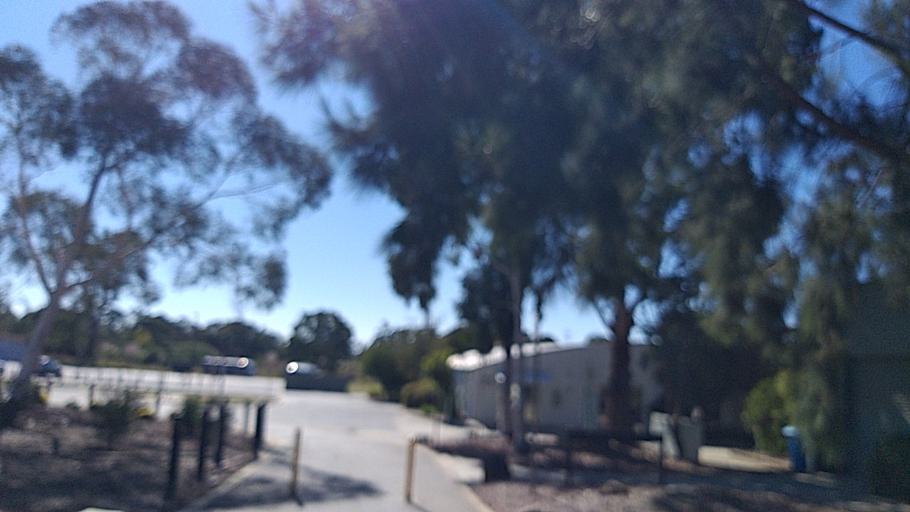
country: AU
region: Australian Capital Territory
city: Kaleen
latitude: -35.2452
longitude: 149.1048
